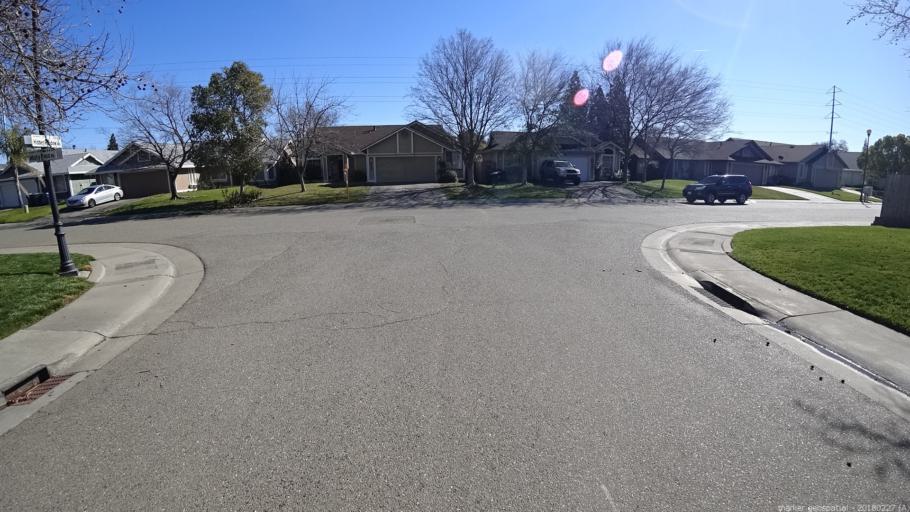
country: US
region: California
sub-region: Sacramento County
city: Antelope
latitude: 38.7229
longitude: -121.3473
